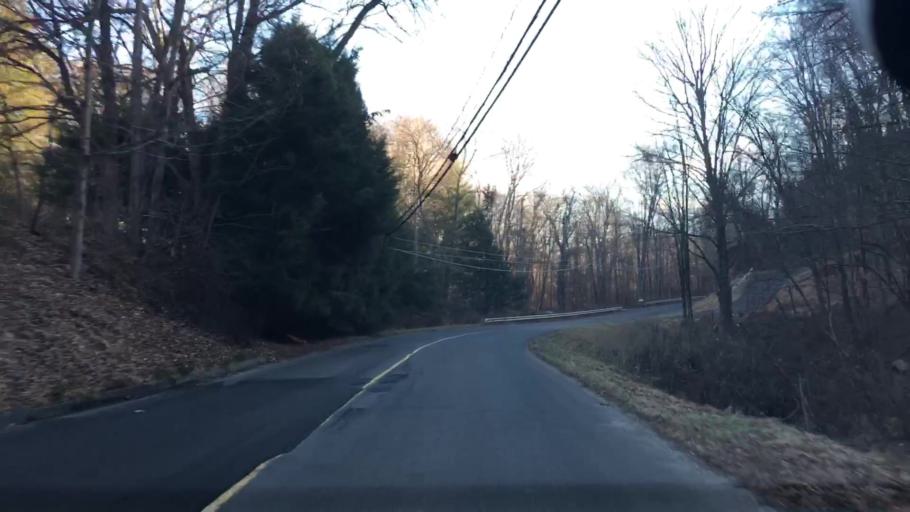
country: US
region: Connecticut
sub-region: Fairfield County
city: Newtown
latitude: 41.4554
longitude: -73.3249
